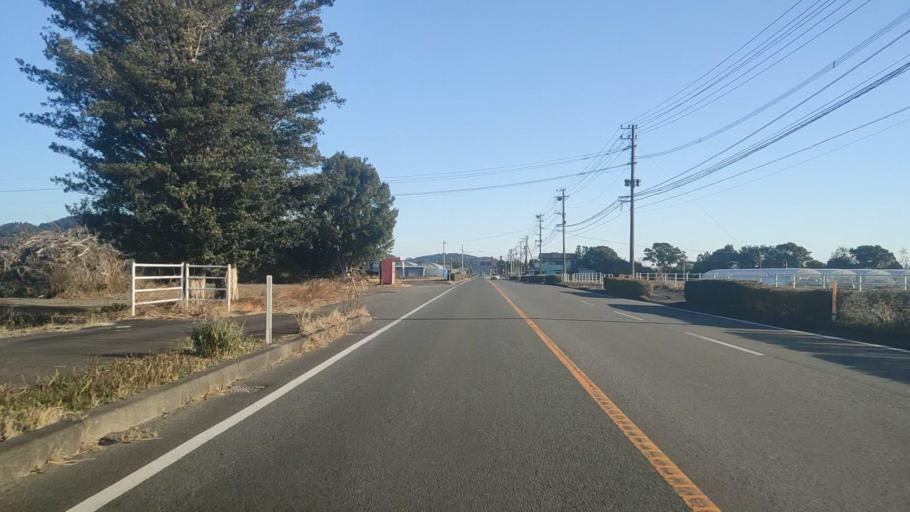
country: JP
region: Miyazaki
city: Takanabe
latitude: 32.3191
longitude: 131.5932
